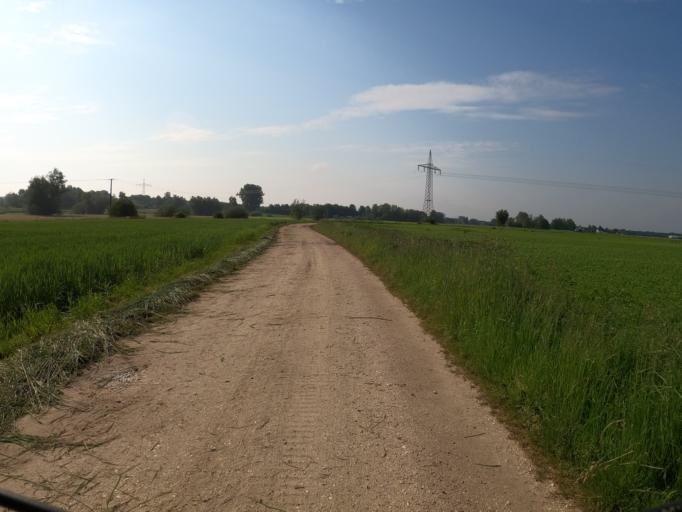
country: DE
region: Bavaria
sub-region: Swabia
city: Nersingen
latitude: 48.3926
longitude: 10.1415
